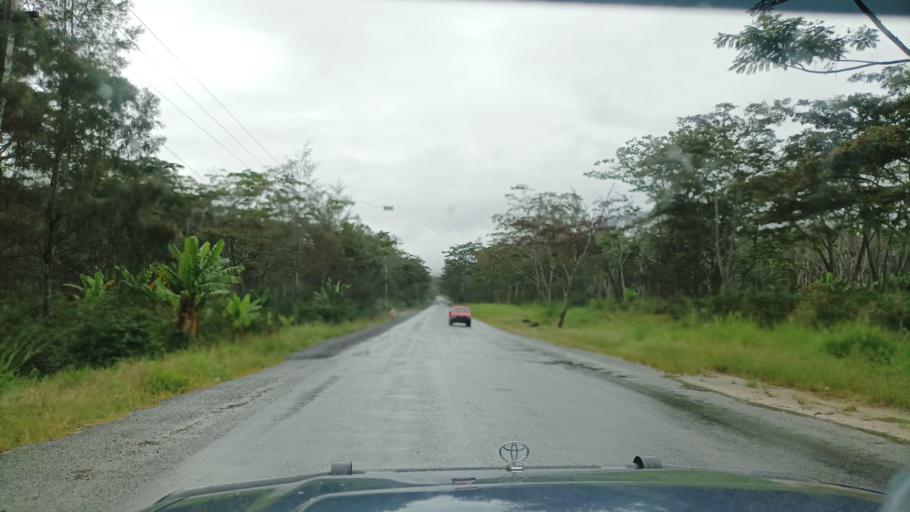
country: PG
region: Western Highlands
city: Rauna
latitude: -5.8332
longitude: 144.3476
